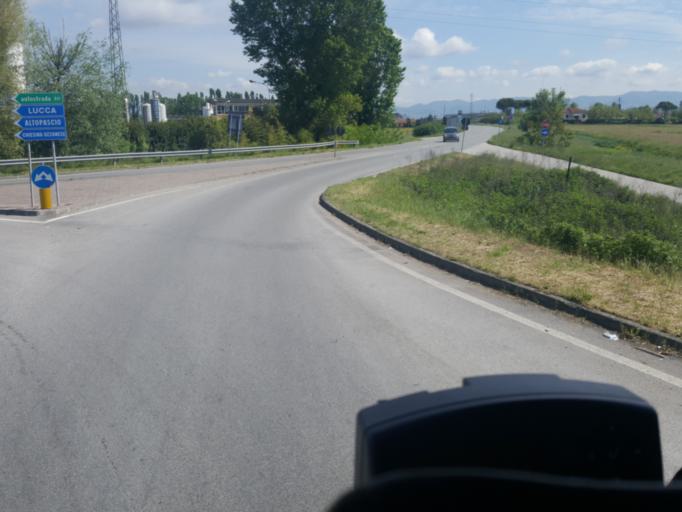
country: IT
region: Tuscany
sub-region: Province of Pisa
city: Santa Croce sull'Arno
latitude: 43.7355
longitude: 10.7748
